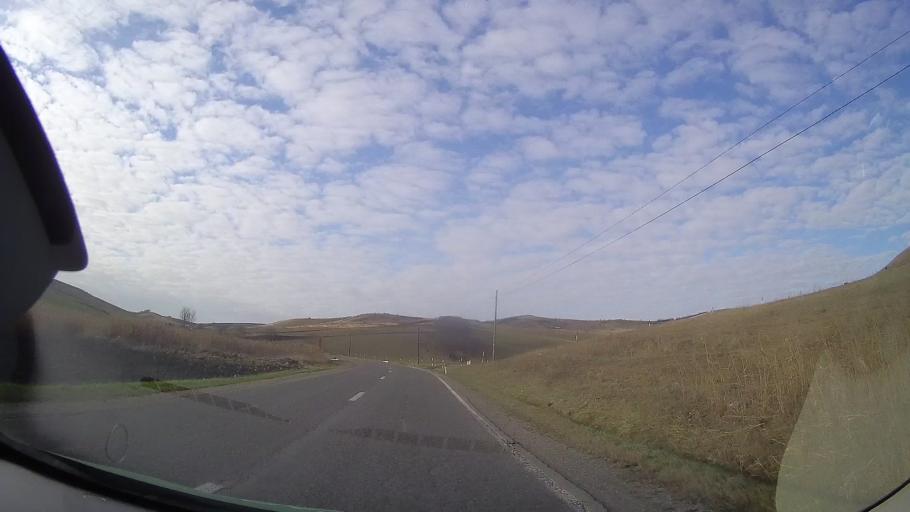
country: RO
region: Cluj
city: Jucu Herghelia
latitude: 46.8117
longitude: 23.8000
